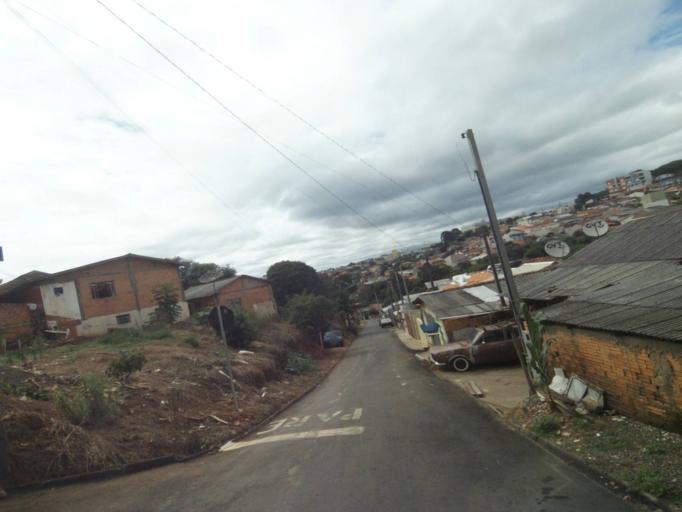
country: BR
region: Parana
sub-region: Telemaco Borba
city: Telemaco Borba
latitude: -24.3309
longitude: -50.6428
